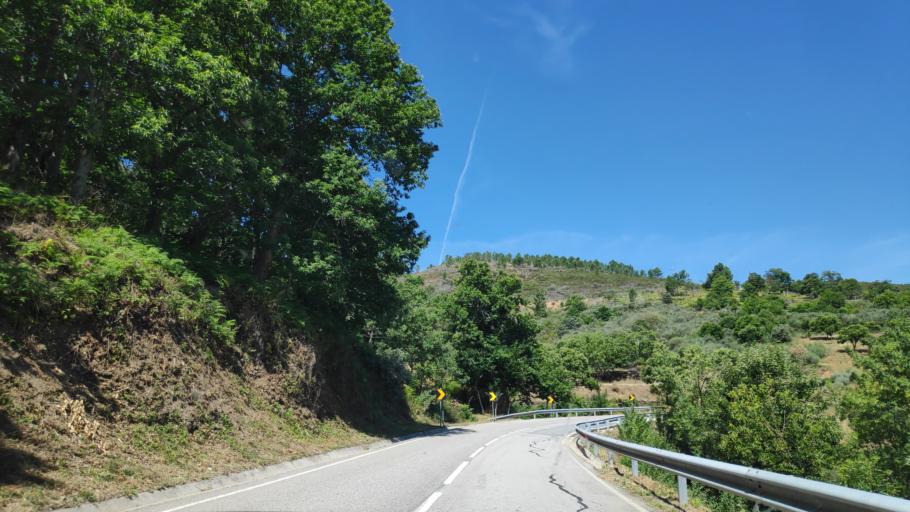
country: PT
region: Braganca
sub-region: Braganca Municipality
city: Braganca
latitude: 41.9106
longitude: -6.7296
